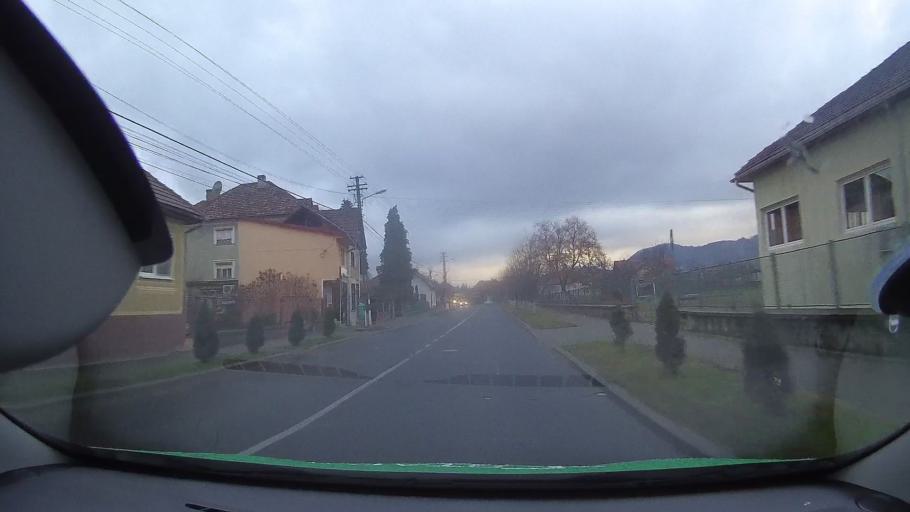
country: RO
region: Hunedoara
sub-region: Municipiul Brad
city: Brad
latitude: 46.1310
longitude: 22.7840
